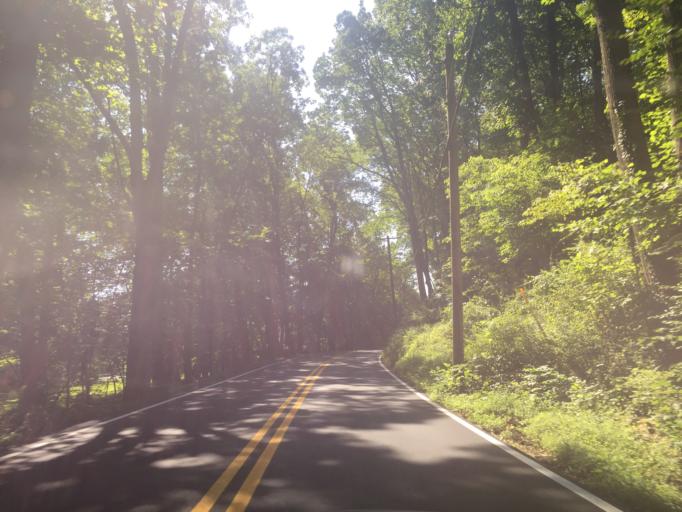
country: US
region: Maryland
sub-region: Baltimore County
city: Mays Chapel
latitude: 39.4123
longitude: -76.6694
